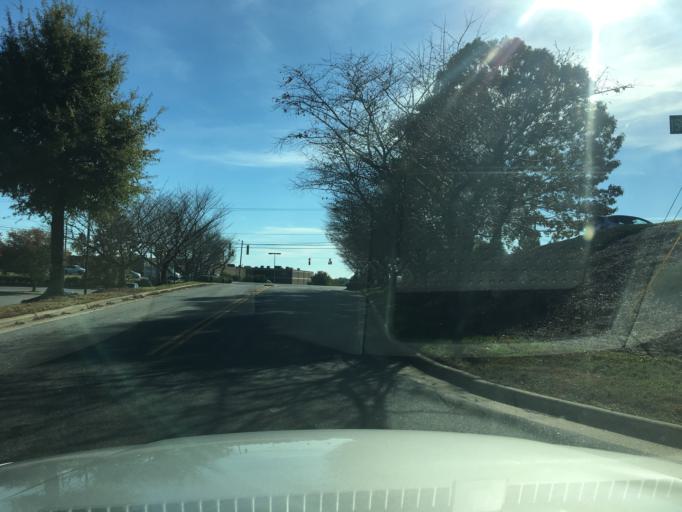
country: US
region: North Carolina
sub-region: Catawba County
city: Hickory
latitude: 35.7051
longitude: -81.2982
